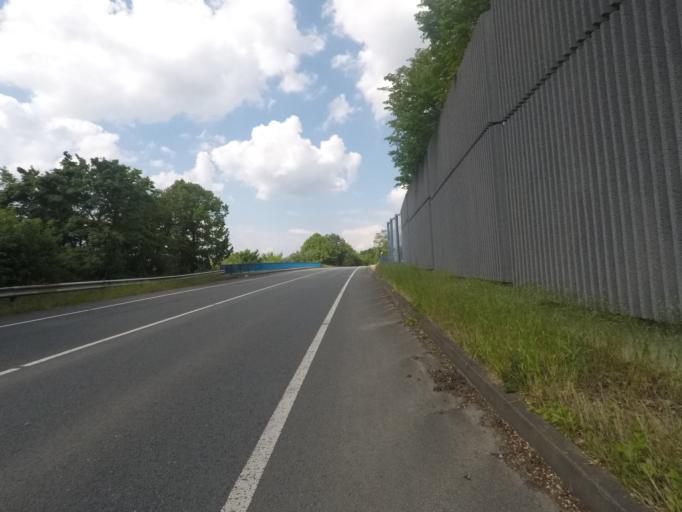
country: DE
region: North Rhine-Westphalia
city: Spenge
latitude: 52.1922
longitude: 8.5183
